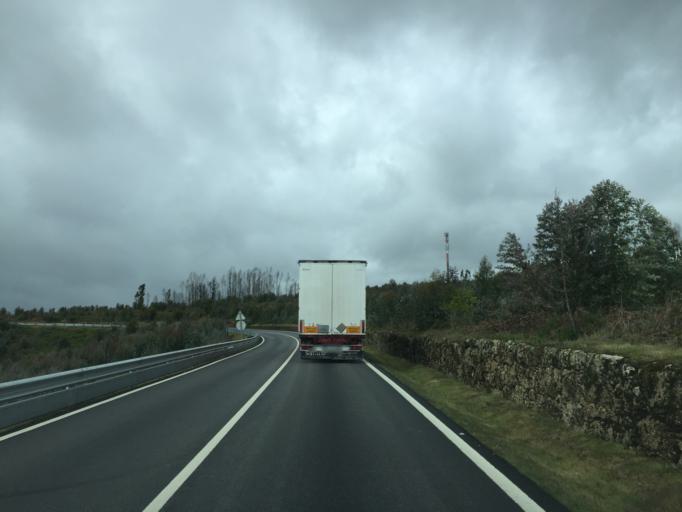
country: PT
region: Coimbra
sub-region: Oliveira do Hospital
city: Oliveira do Hospital
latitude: 40.3236
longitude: -7.9279
